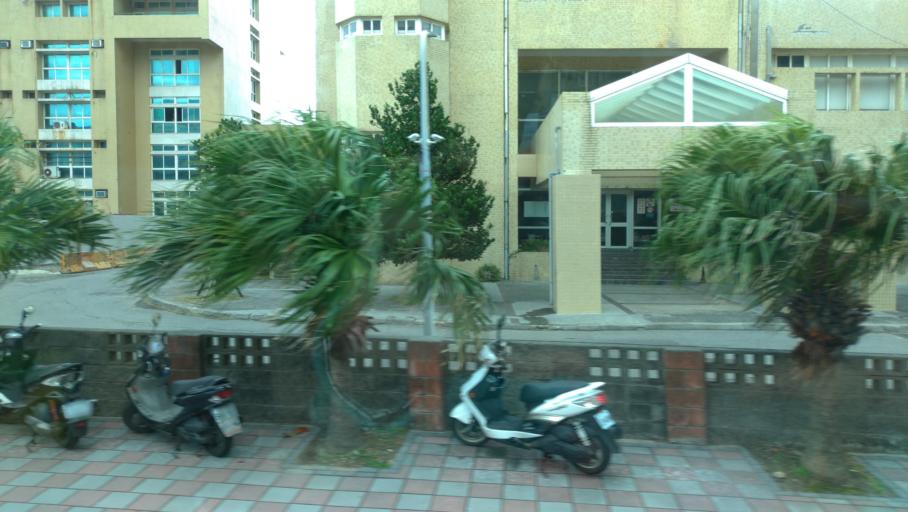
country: TW
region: Taiwan
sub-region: Keelung
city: Keelung
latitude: 25.1503
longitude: 121.7806
